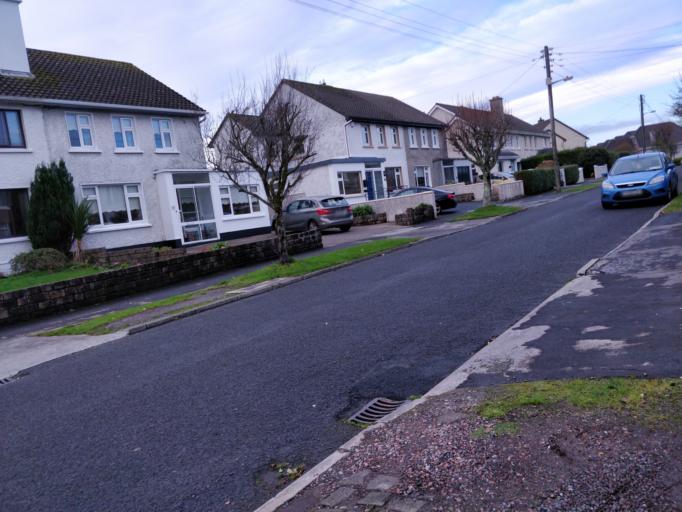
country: IE
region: Connaught
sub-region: County Galway
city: Gaillimh
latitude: 53.2607
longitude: -9.0874
